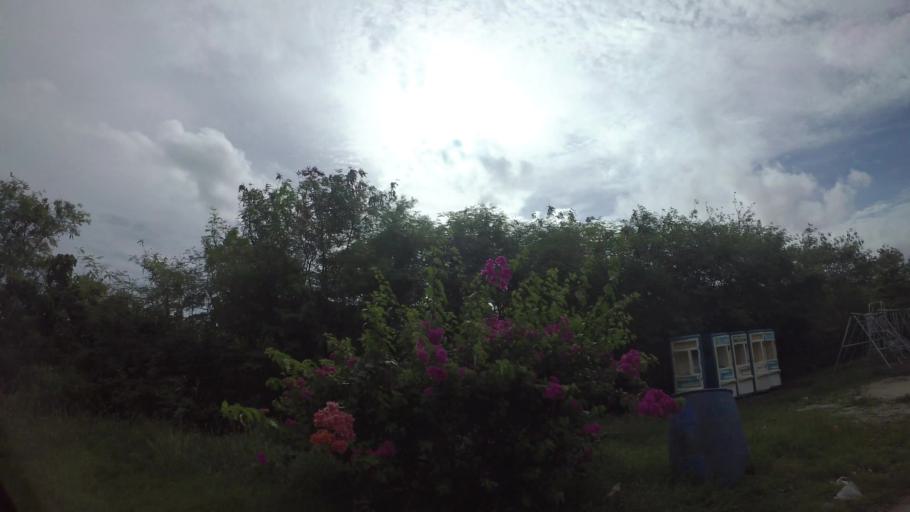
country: TH
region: Rayong
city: Rayong
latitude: 12.6633
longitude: 101.2796
